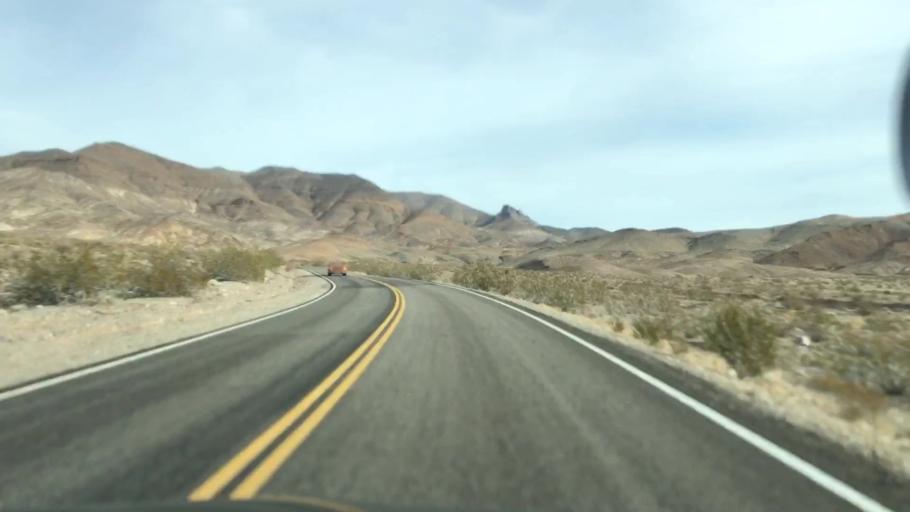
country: US
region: Nevada
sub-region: Nye County
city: Beatty
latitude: 36.7292
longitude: -116.9737
